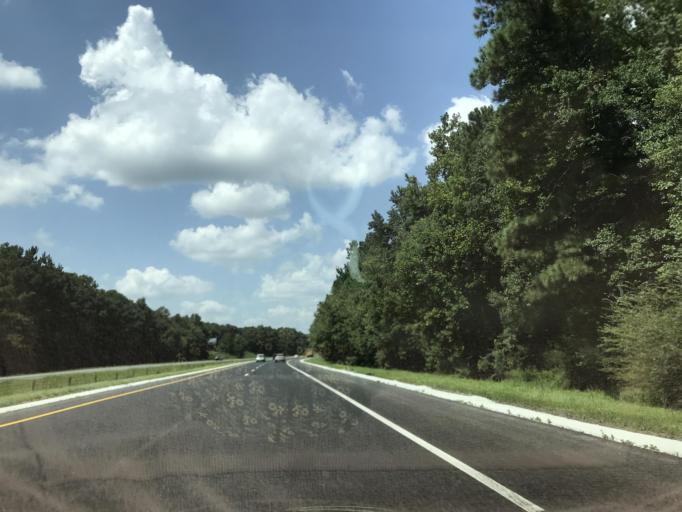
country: US
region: North Carolina
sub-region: Duplin County
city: Warsaw
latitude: 34.9559
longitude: -78.0981
